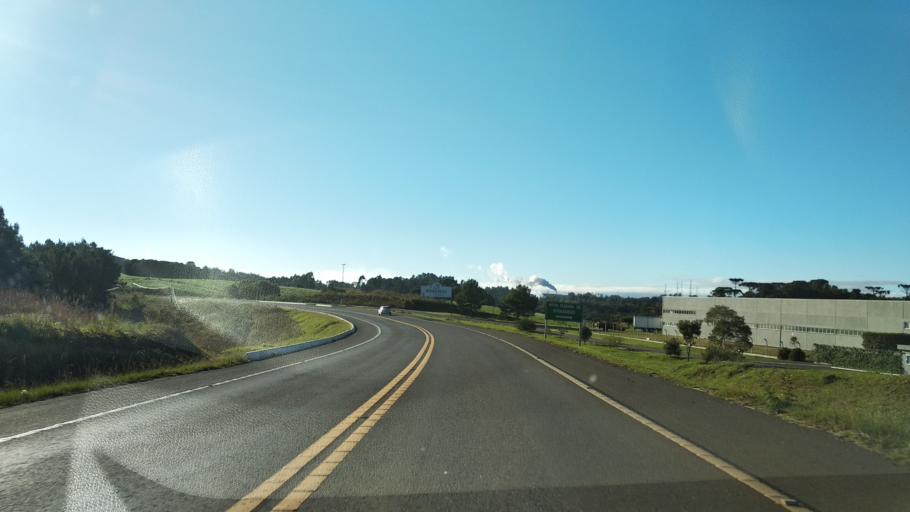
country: BR
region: Santa Catarina
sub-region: Lages
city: Lages
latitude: -27.7968
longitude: -50.3964
